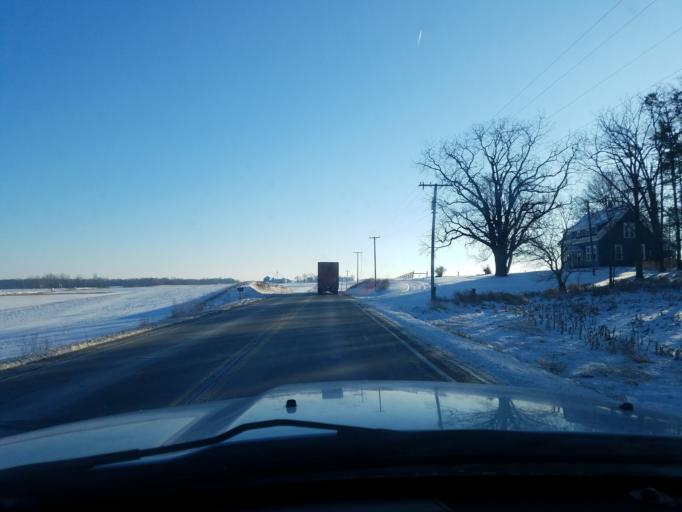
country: US
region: Indiana
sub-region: Noble County
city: Albion
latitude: 41.4531
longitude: -85.4504
